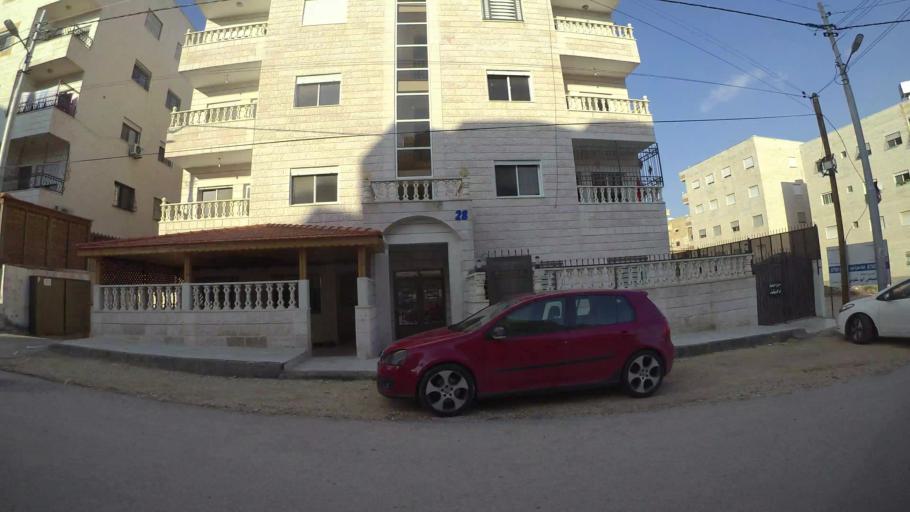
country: JO
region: Amman
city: Amman
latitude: 31.9797
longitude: 35.9377
